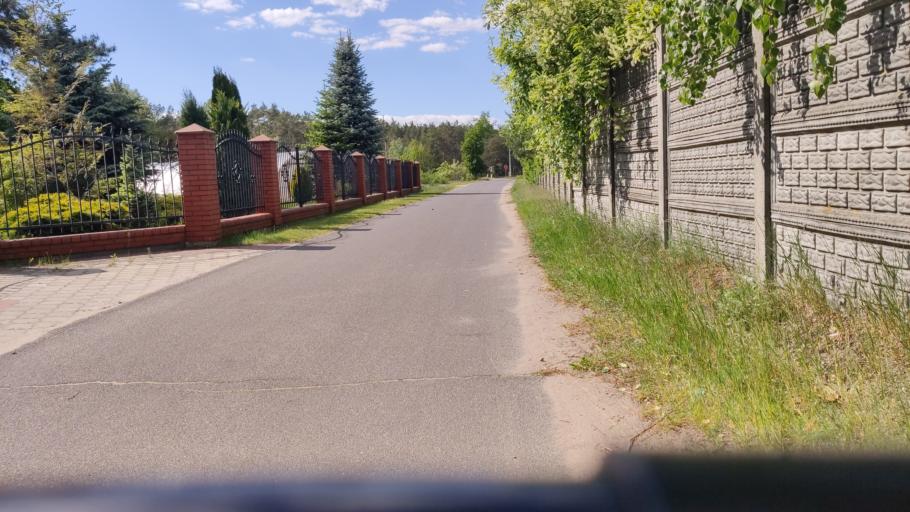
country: PL
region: Kujawsko-Pomorskie
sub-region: Wloclawek
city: Wloclawek
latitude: 52.6039
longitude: 19.0770
